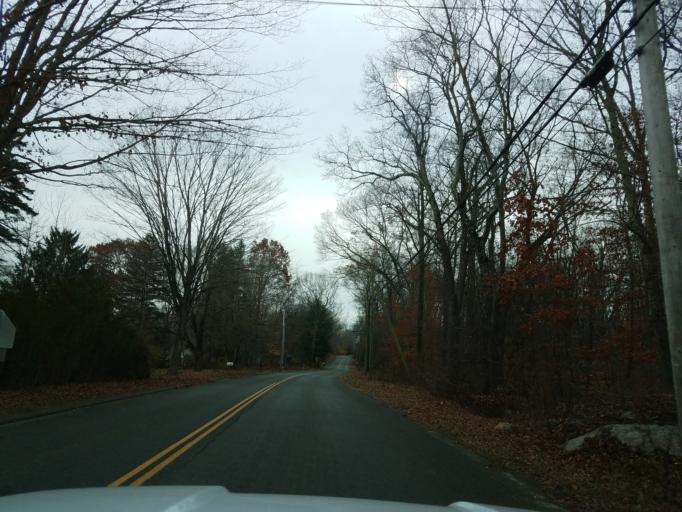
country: US
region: Connecticut
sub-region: New Haven County
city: North Branford
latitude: 41.3359
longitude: -72.7234
